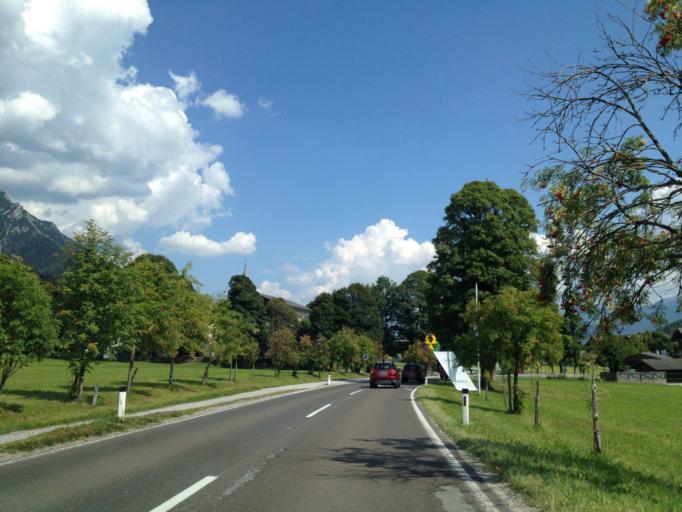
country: AT
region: Styria
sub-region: Politischer Bezirk Liezen
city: Schladming
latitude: 47.4221
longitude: 13.6497
